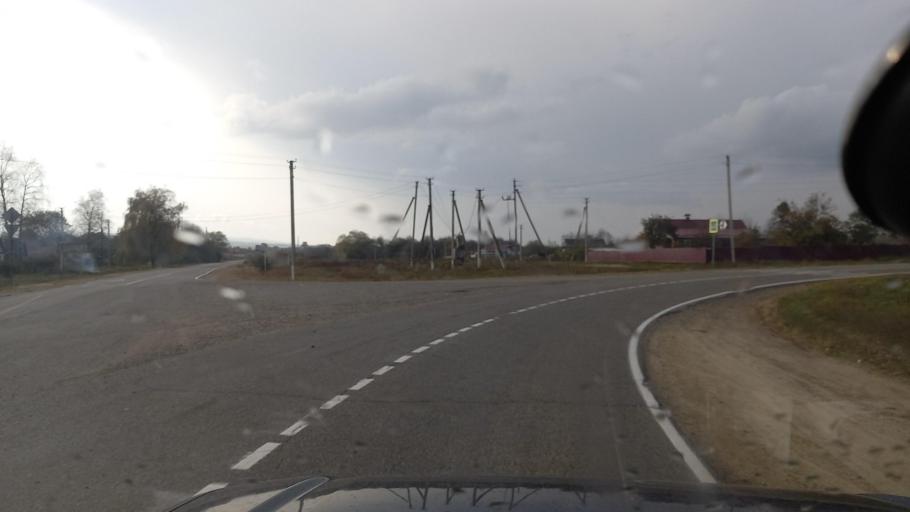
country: RU
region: Krasnodarskiy
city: Gubskaya
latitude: 44.3195
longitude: 40.6074
